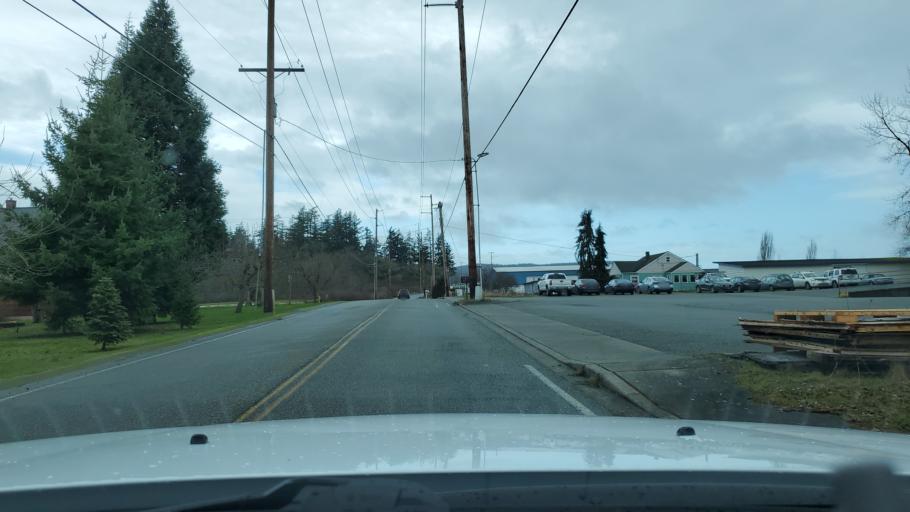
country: US
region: Washington
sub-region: Skagit County
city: Anacortes
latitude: 48.4584
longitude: -122.5484
